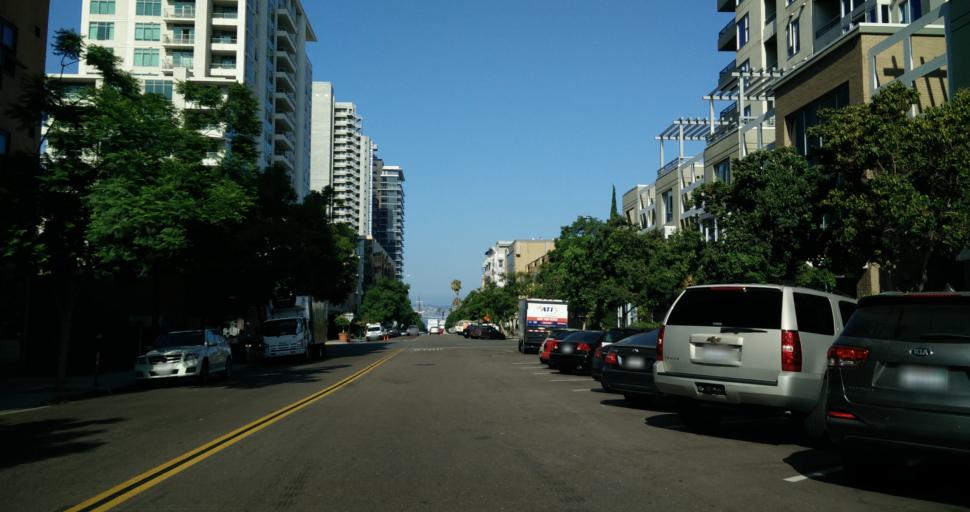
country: US
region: California
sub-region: San Diego County
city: San Diego
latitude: 32.7210
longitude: -117.1658
